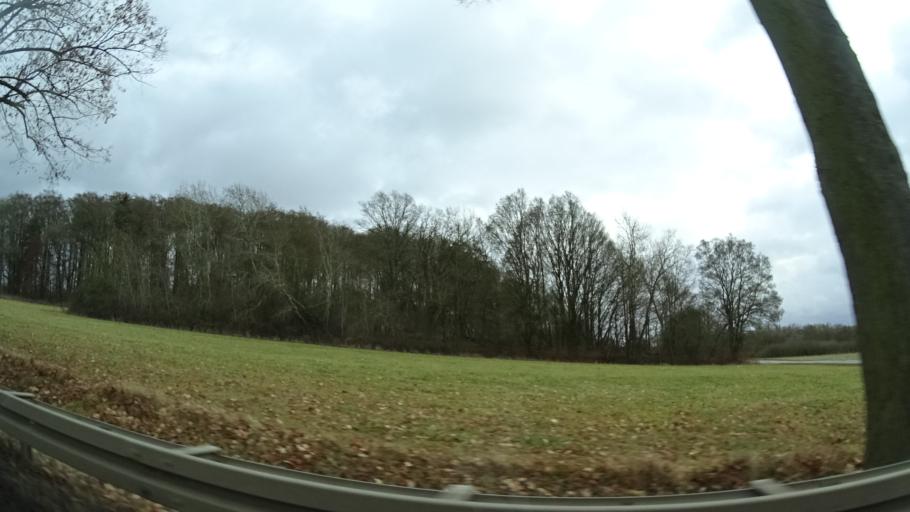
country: DE
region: Hesse
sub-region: Regierungsbezirk Giessen
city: Lauterbach
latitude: 50.6487
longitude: 9.4169
